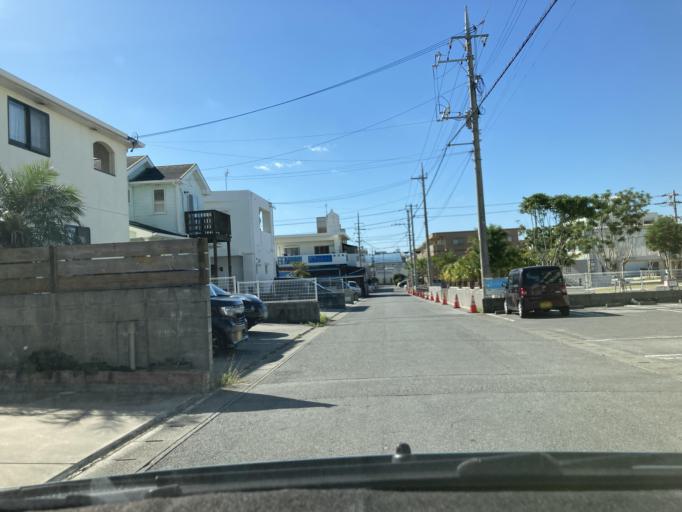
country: JP
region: Okinawa
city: Okinawa
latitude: 26.3465
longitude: 127.8283
